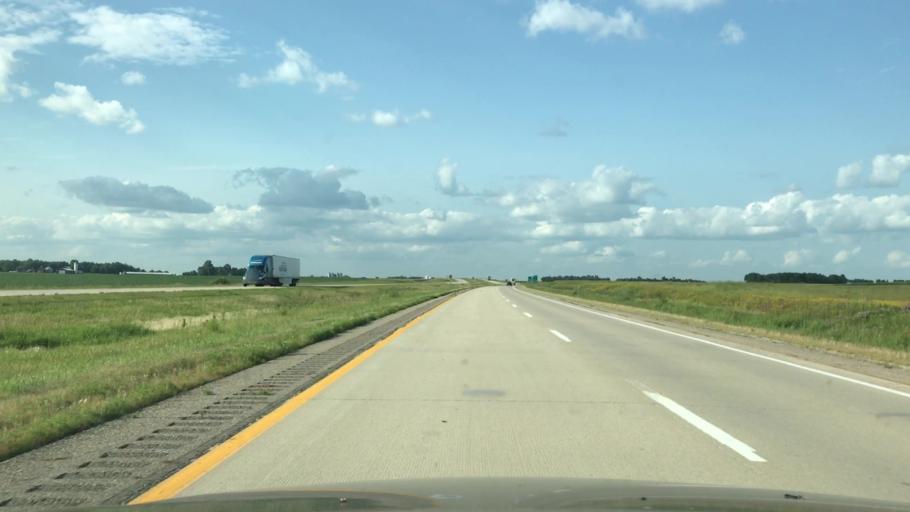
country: US
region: Iowa
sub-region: Osceola County
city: Sibley
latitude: 43.4223
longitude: -95.7159
